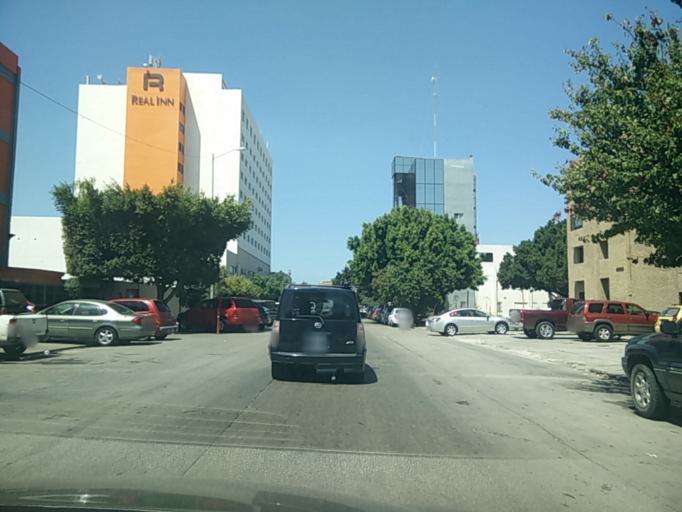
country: MX
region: Baja California
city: Tijuana
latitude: 32.5245
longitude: -117.0152
